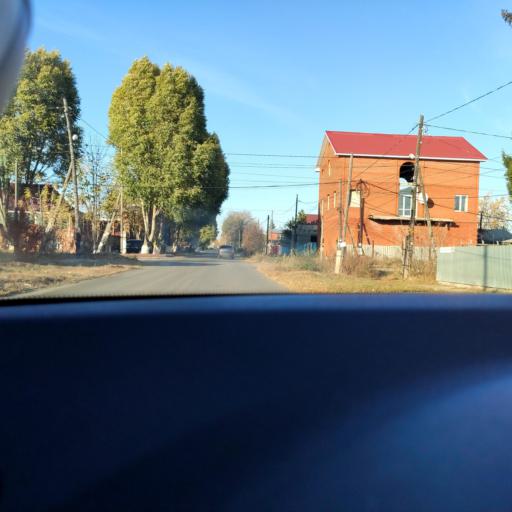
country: RU
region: Samara
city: Petra-Dubrava
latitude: 53.2508
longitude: 50.3286
